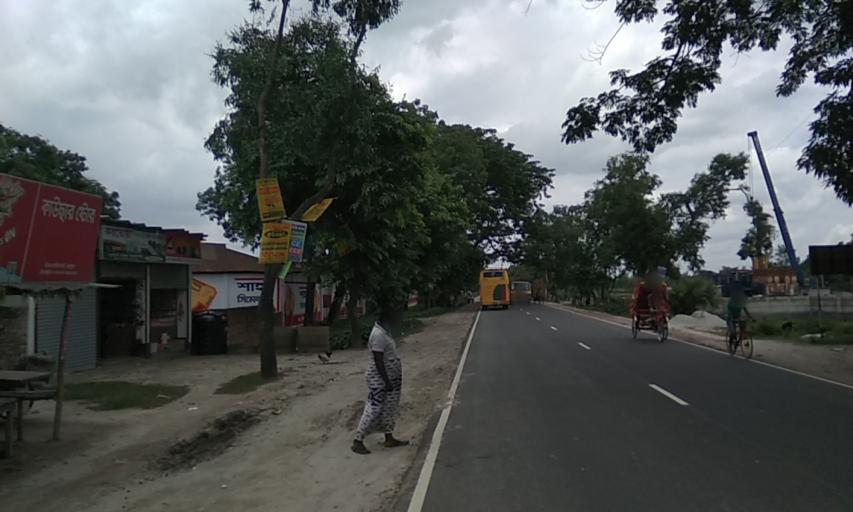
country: BD
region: Rangpur Division
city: Rangpur
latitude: 25.7976
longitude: 89.1944
